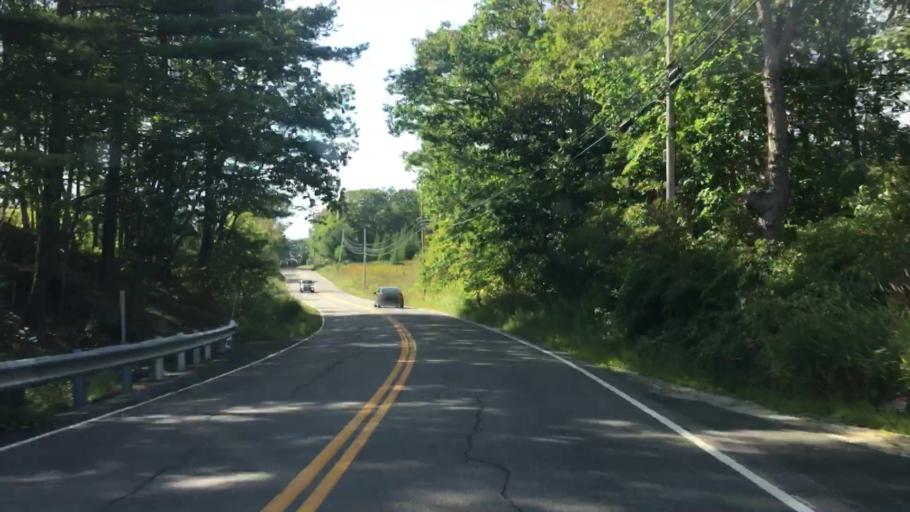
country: US
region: Maine
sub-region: Sagadahoc County
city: North Bath
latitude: 43.9327
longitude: -69.8654
